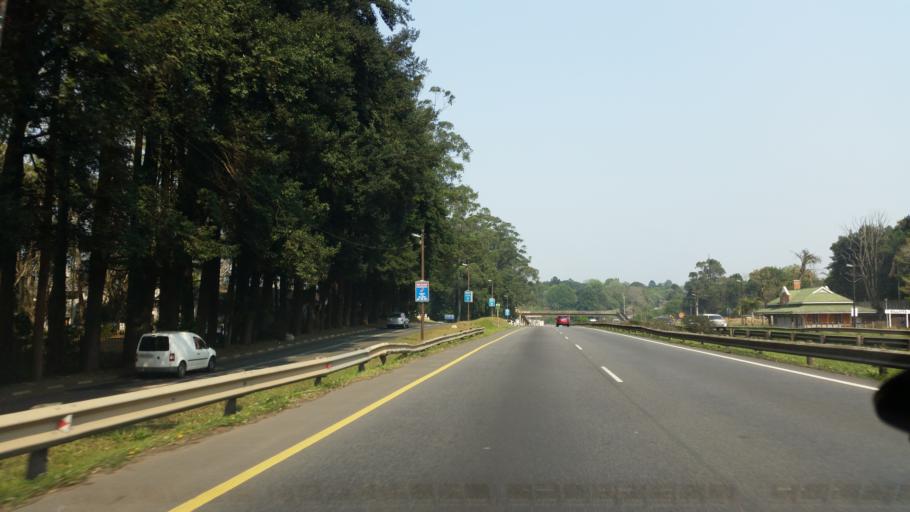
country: ZA
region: KwaZulu-Natal
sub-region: eThekwini Metropolitan Municipality
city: Mpumalanga
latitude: -29.7934
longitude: 30.8018
